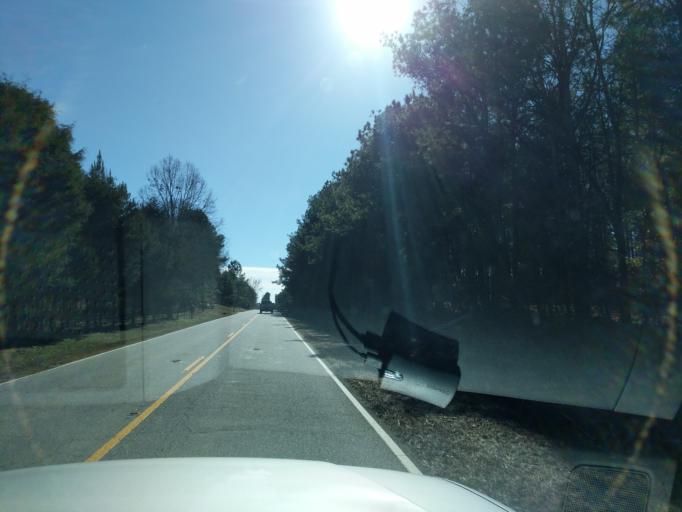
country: US
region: South Carolina
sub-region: Greenwood County
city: Ninety Six
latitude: 34.1598
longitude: -81.8528
